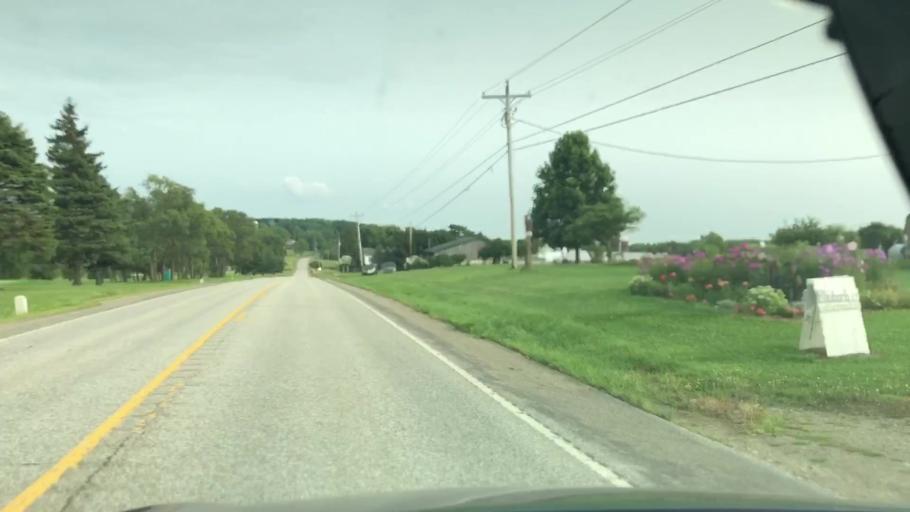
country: US
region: Pennsylvania
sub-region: Erie County
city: Union City
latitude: 41.8573
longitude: -79.8289
